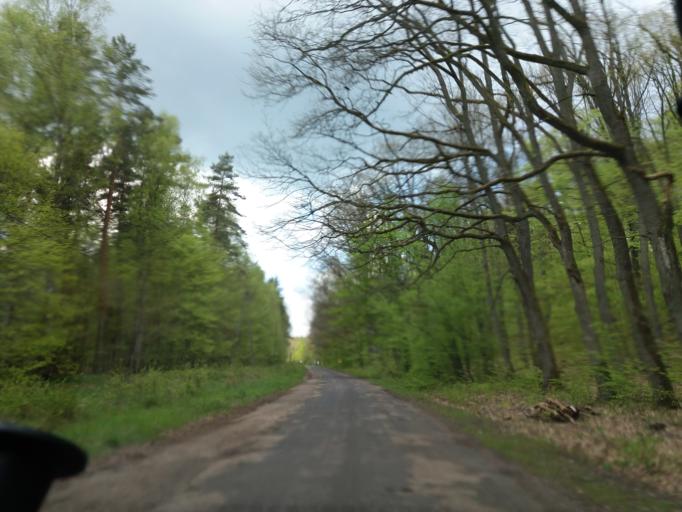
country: PL
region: West Pomeranian Voivodeship
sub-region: Powiat choszczenski
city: Drawno
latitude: 53.1504
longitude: 15.8753
